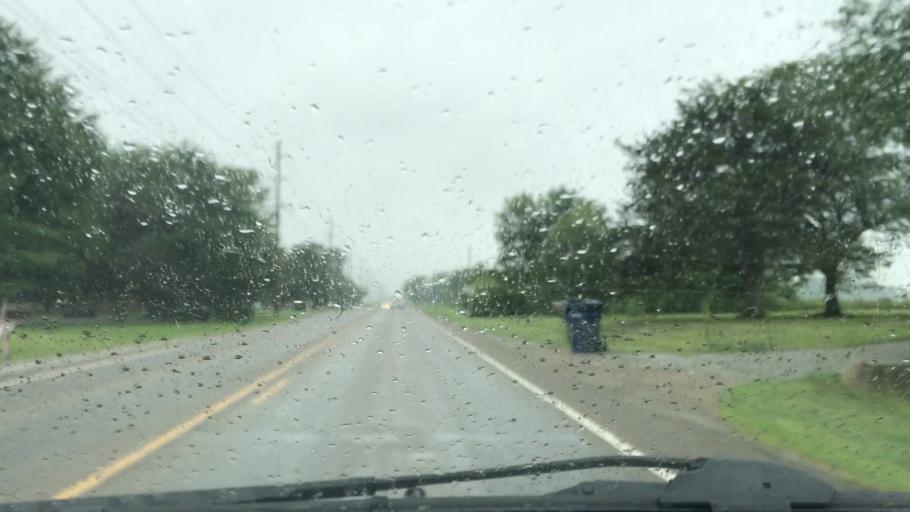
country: US
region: Indiana
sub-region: Hamilton County
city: Westfield
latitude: 40.1051
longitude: -86.1528
